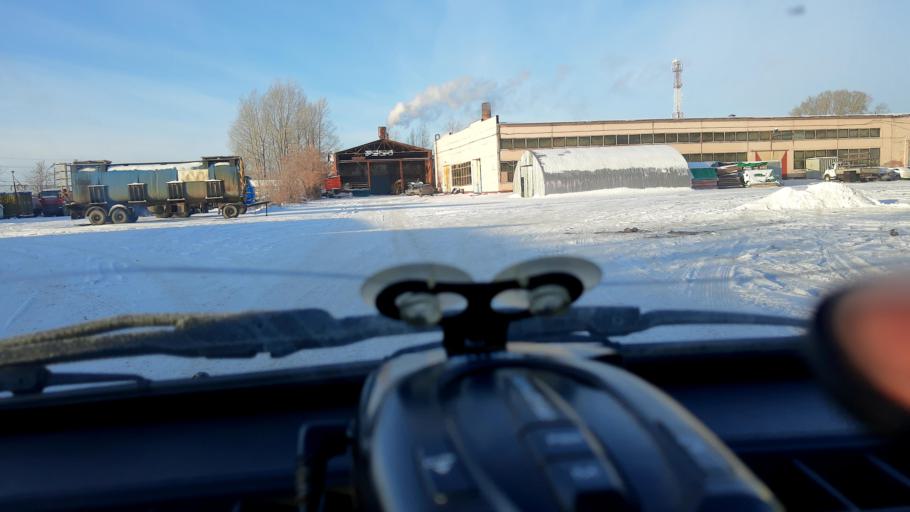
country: RU
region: Bashkortostan
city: Avdon
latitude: 54.6069
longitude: 55.8443
